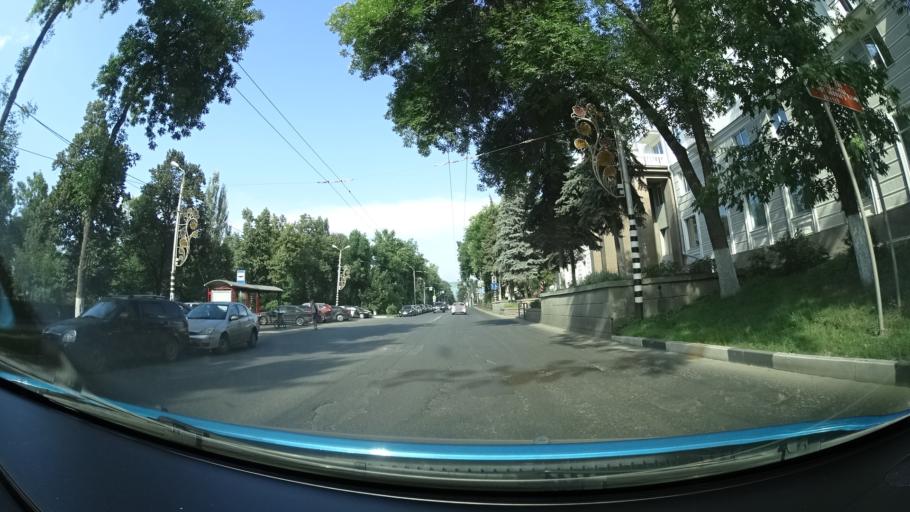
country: RU
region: Samara
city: Samara
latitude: 53.2056
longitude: 50.1096
